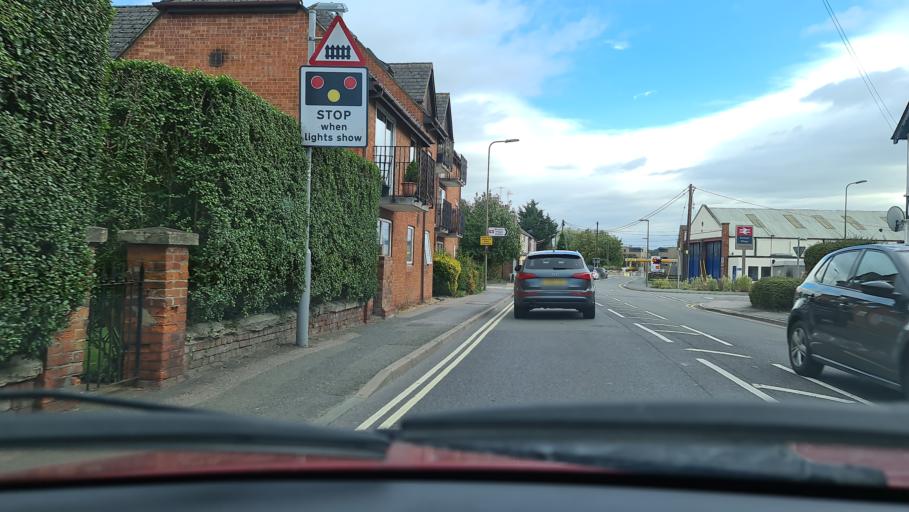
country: GB
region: England
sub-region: Oxfordshire
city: Bicester
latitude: 51.8948
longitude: -1.1483
